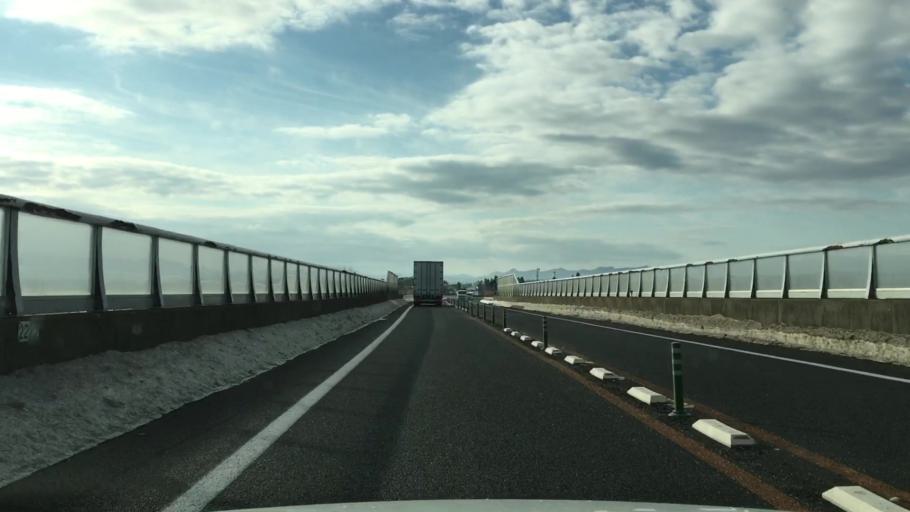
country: JP
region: Akita
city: Odate
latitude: 40.2857
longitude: 140.5411
